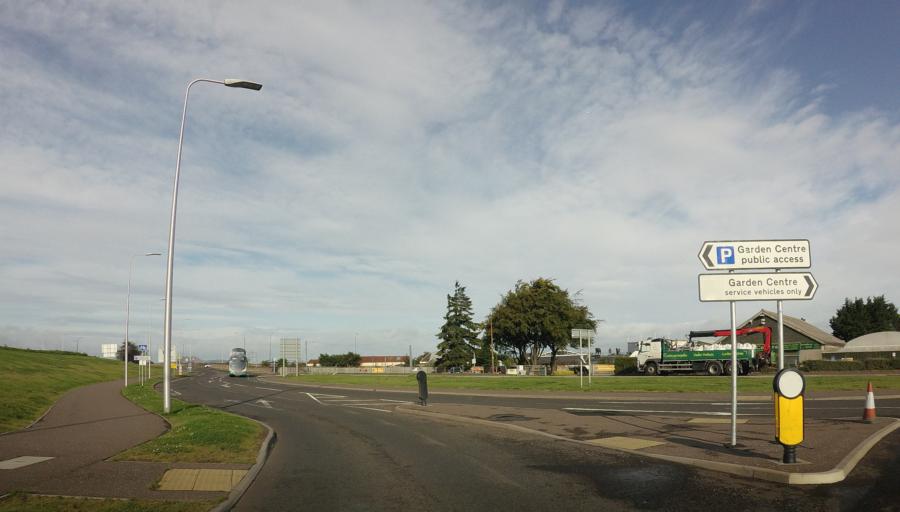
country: GB
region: Scotland
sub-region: East Lothian
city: Prestonpans
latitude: 55.9424
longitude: -3.0054
